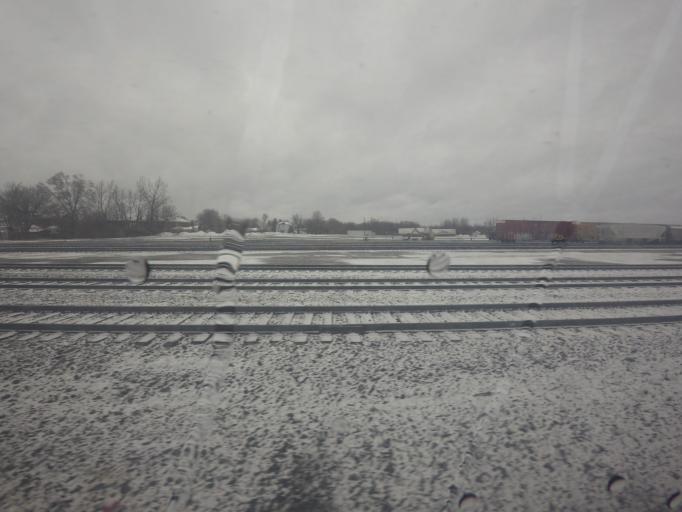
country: CA
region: Ontario
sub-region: Lanark County
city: Smiths Falls
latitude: 44.9060
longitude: -76.0176
